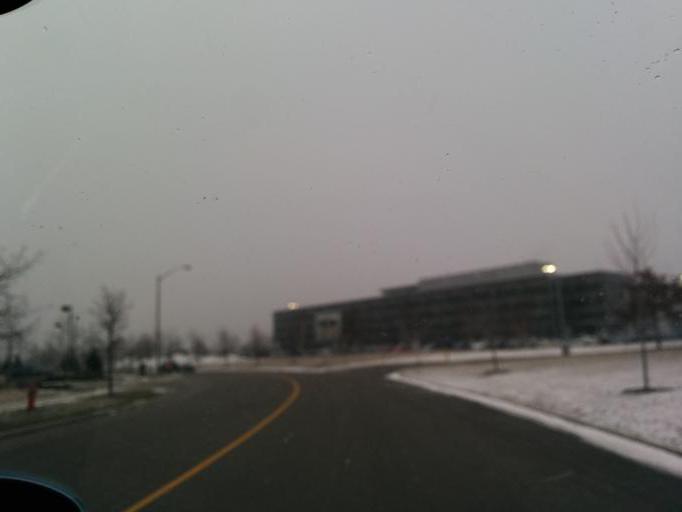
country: CA
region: Ontario
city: Brampton
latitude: 43.6200
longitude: -79.7708
